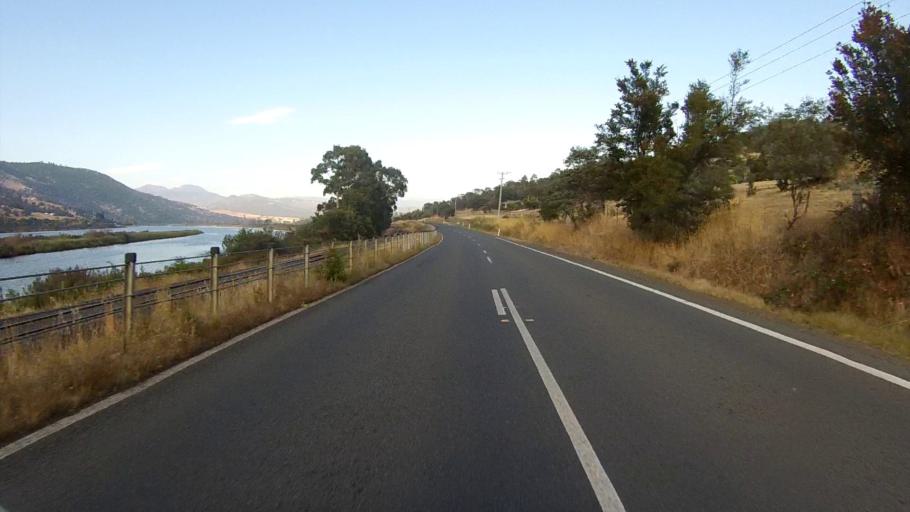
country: AU
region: Tasmania
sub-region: Glenorchy
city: Granton
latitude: -42.7511
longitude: 147.1507
